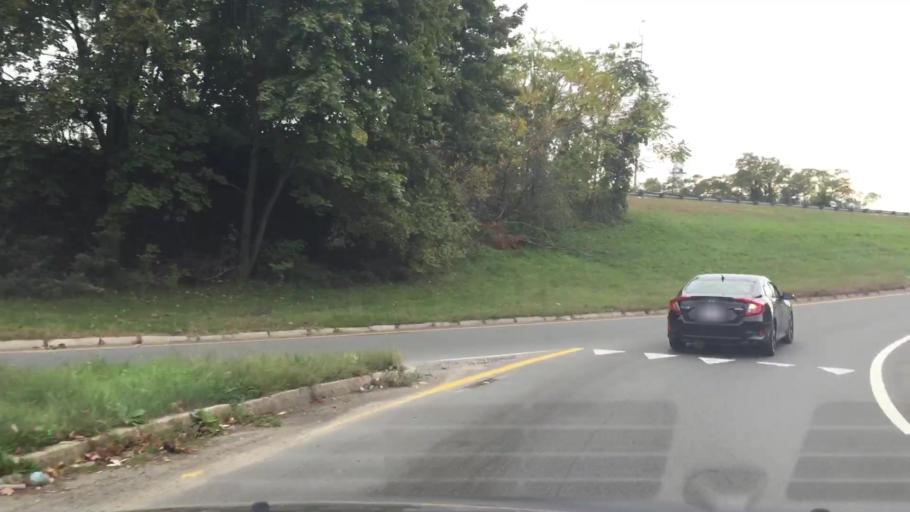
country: US
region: Massachusetts
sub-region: Middlesex County
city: Lowell
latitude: 42.6346
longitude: -71.3114
